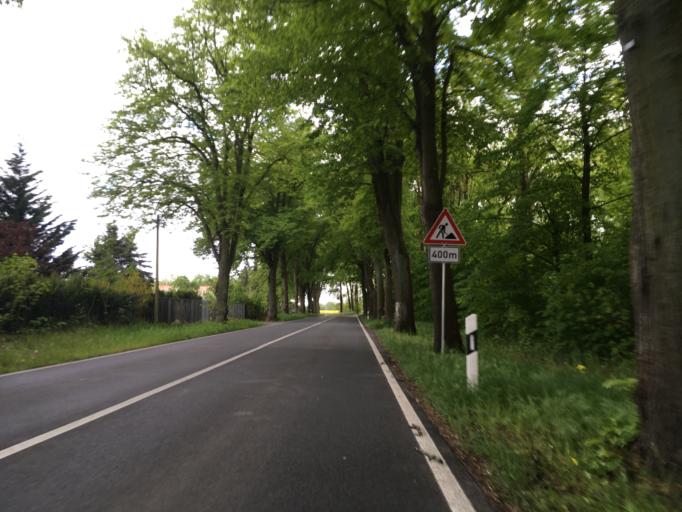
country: DE
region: Brandenburg
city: Ahrensfelde
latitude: 52.6212
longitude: 13.6113
